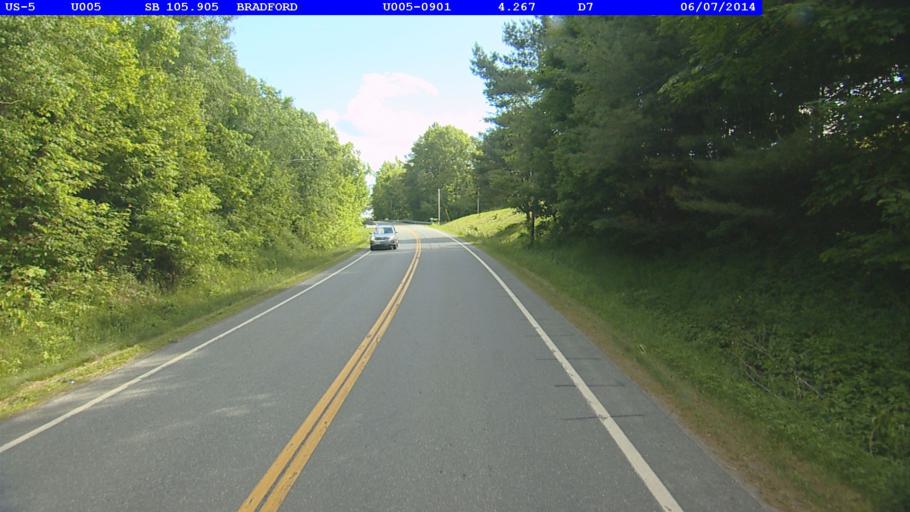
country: US
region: New Hampshire
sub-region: Grafton County
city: Haverhill
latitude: 44.0139
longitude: -72.1061
